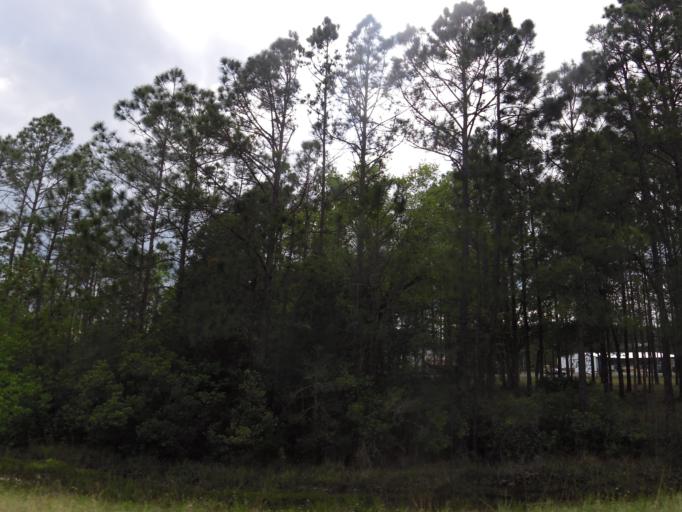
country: US
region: Georgia
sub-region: Charlton County
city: Folkston
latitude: 30.8755
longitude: -82.0150
